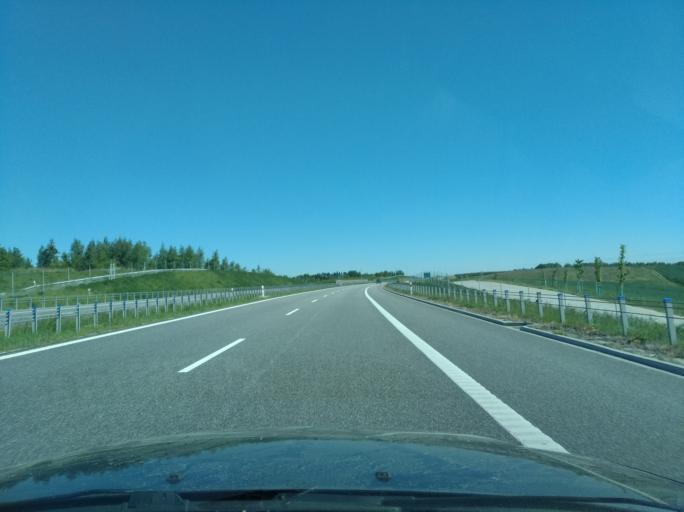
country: PL
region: Subcarpathian Voivodeship
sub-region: Rzeszow
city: Przybyszowka
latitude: 50.0563
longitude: 21.9244
